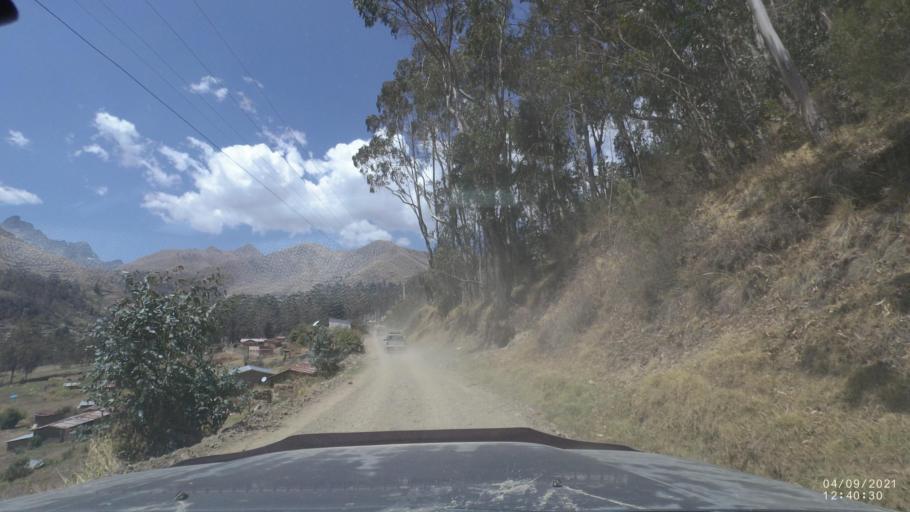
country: BO
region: Cochabamba
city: Colchani
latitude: -17.2297
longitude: -66.4962
